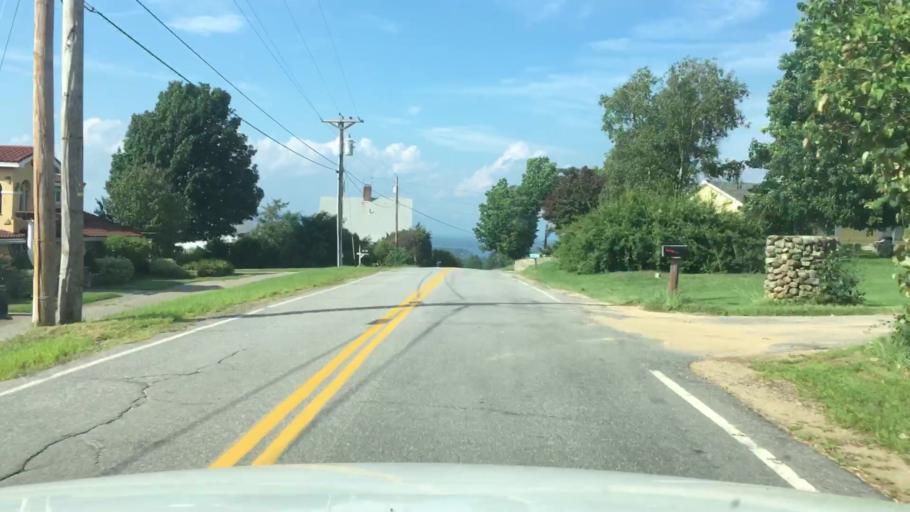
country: US
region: New Hampshire
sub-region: Belknap County
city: Gilford
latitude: 43.5558
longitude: -71.4156
